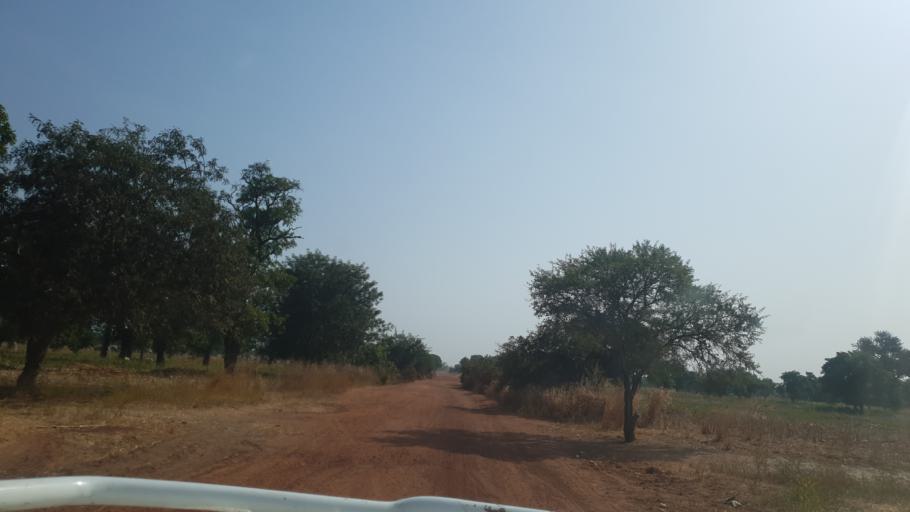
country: ML
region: Koulikoro
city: Dioila
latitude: 12.6686
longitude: -6.6791
